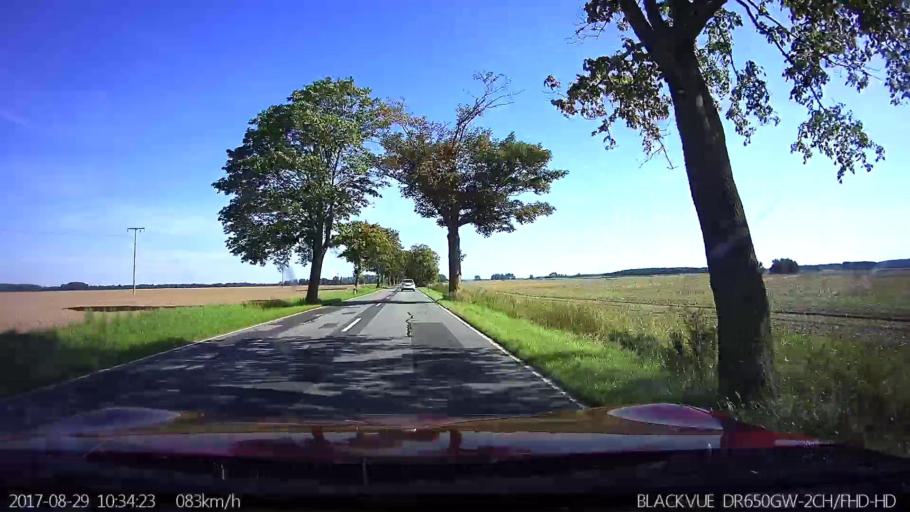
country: DE
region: Mecklenburg-Vorpommern
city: Tribsees
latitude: 54.1264
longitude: 12.7859
